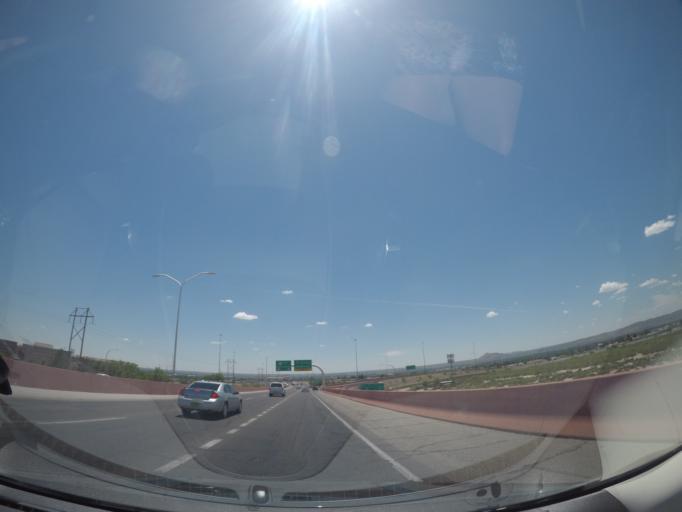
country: US
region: New Mexico
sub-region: Dona Ana County
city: Las Cruces
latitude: 32.3507
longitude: -106.7667
